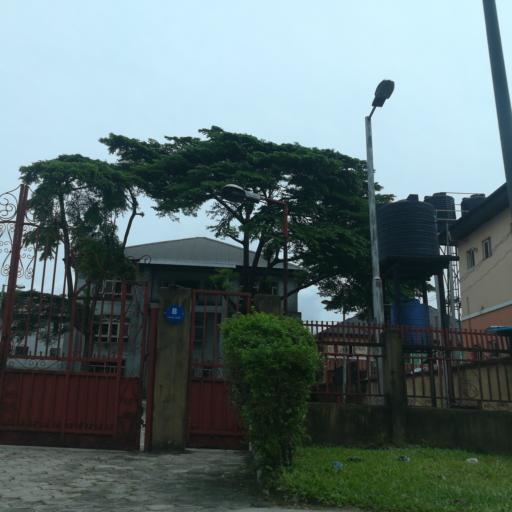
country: NG
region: Rivers
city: Port Harcourt
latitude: 4.8002
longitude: 7.0020
